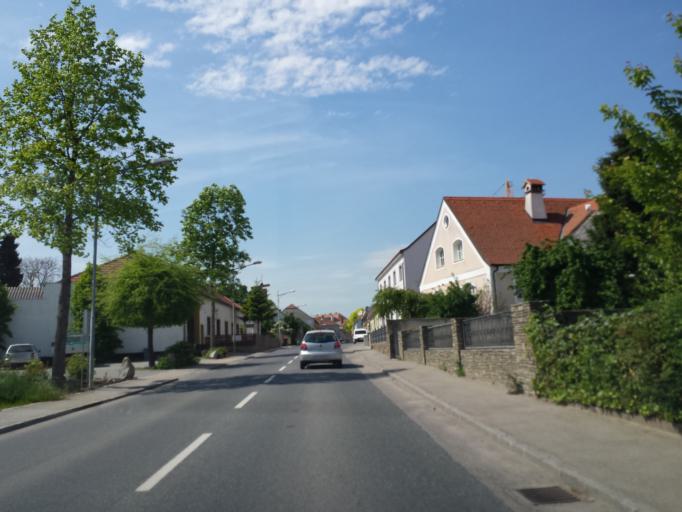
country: AT
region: Lower Austria
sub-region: Politischer Bezirk Tulln
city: Atzenbrugg
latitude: 48.2981
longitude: 15.8960
